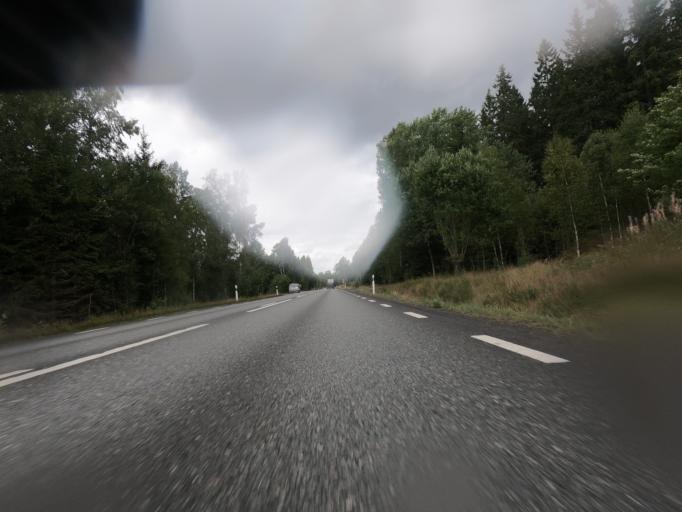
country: SE
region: Joenkoeping
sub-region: Savsjo Kommun
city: Vrigstad
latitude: 57.4339
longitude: 14.3187
